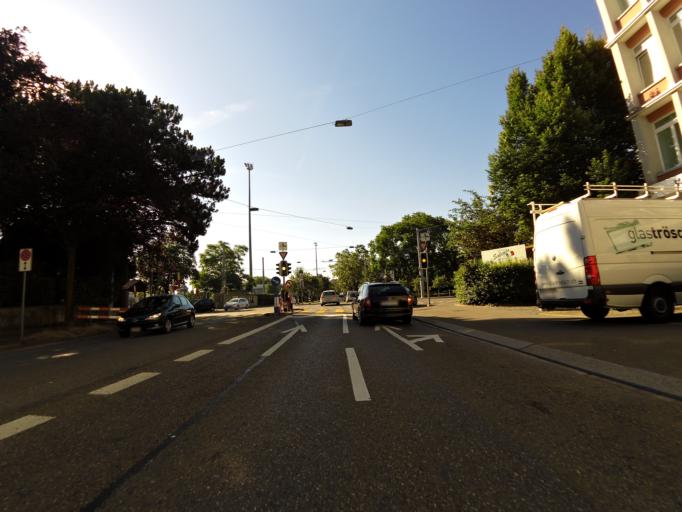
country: CH
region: Zurich
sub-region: Bezirk Zuerich
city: Zuerich (Kreis 9) / Albisrieden
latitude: 47.3796
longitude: 8.4949
